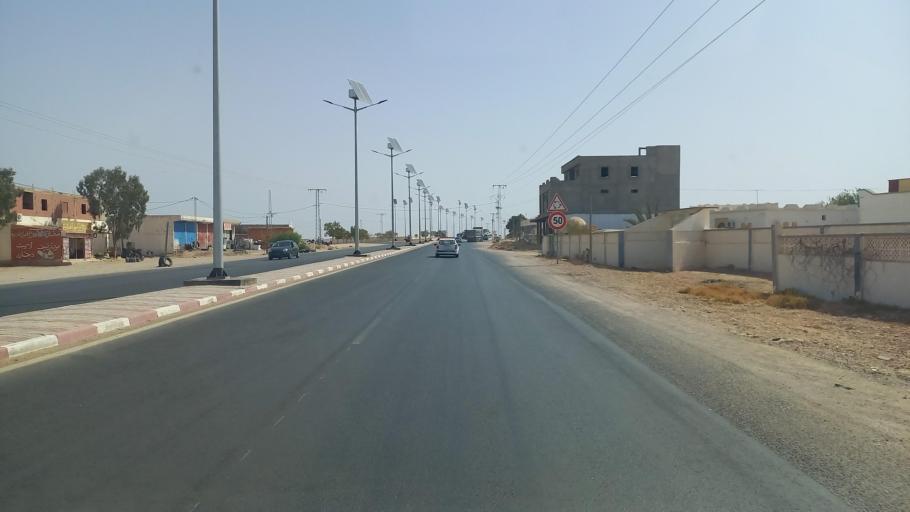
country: TN
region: Madanin
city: Medenine
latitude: 33.3593
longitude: 10.5531
